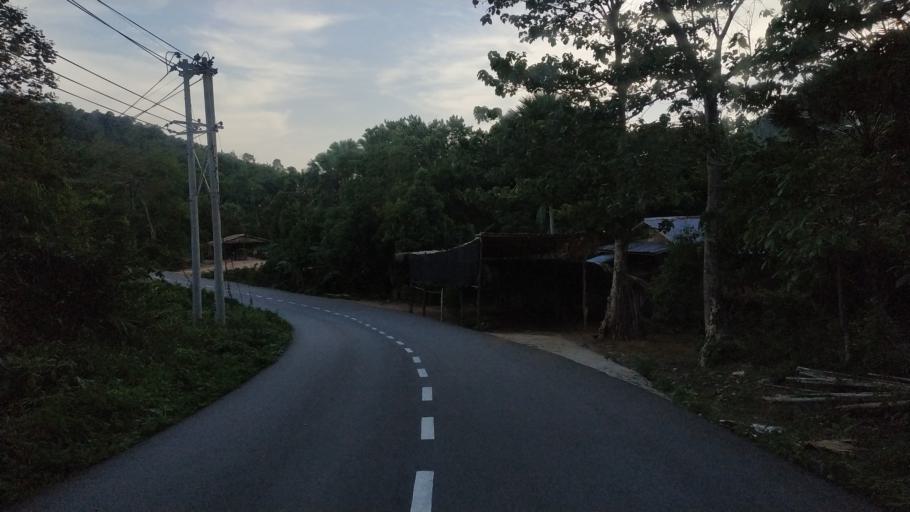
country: MM
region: Mon
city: Kyaikto
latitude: 17.4263
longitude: 97.0827
